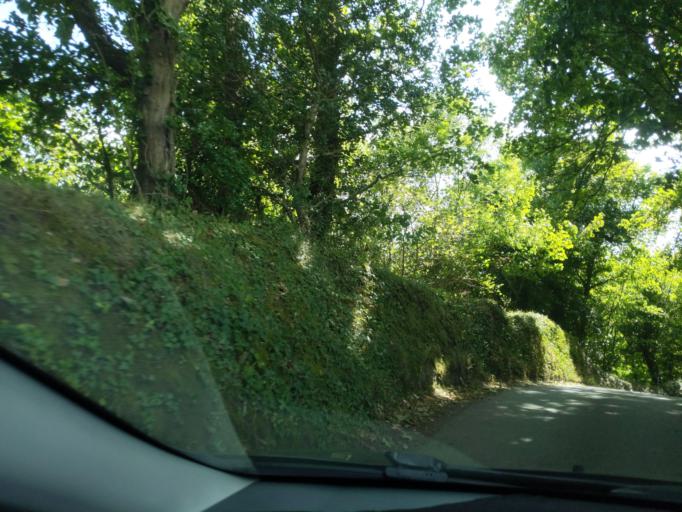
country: GB
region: England
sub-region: Cornwall
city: Torpoint
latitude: 50.3637
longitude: -4.2375
